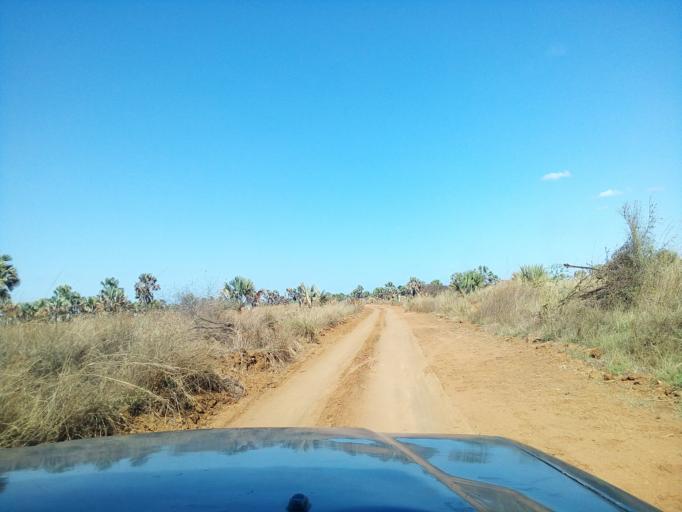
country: MG
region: Boeny
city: Mahajanga
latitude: -15.8516
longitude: 46.1547
